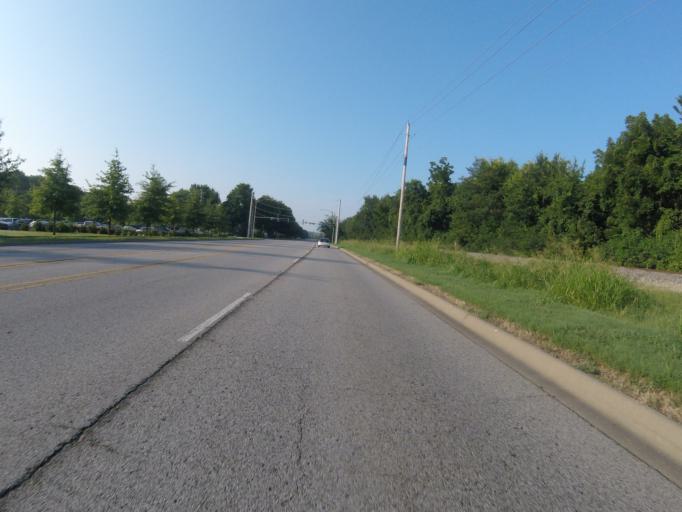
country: US
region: Arkansas
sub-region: Washington County
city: Johnson
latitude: 36.1090
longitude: -94.1636
